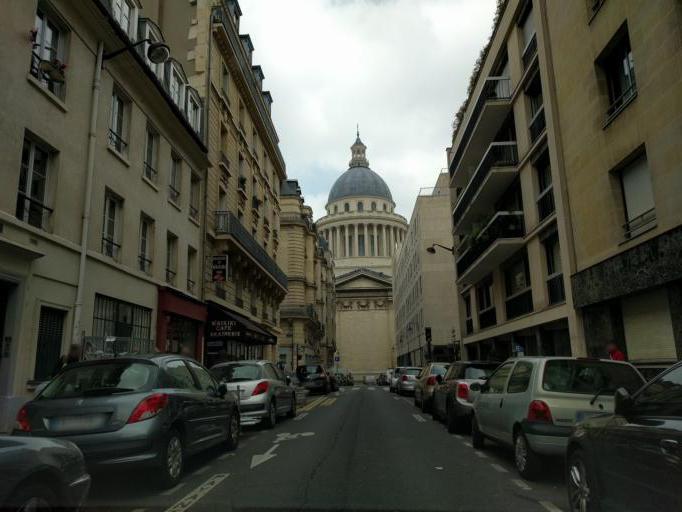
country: FR
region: Ile-de-France
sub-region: Paris
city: Paris
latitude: 48.8446
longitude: 2.3453
